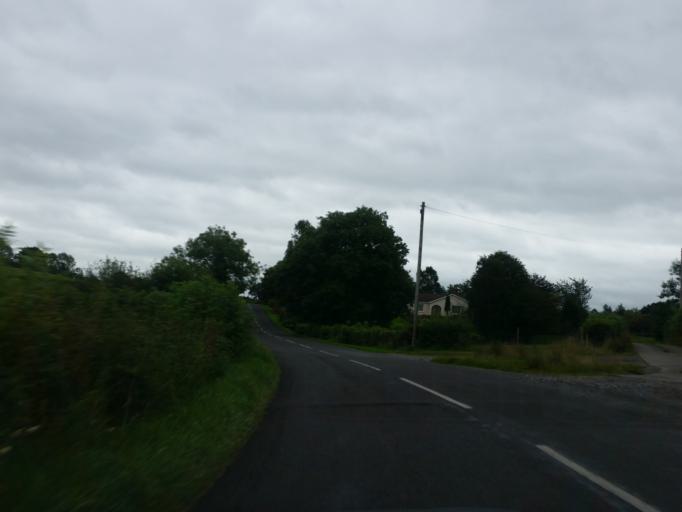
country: GB
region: Northern Ireland
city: Lisnaskea
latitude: 54.3297
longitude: -7.4813
